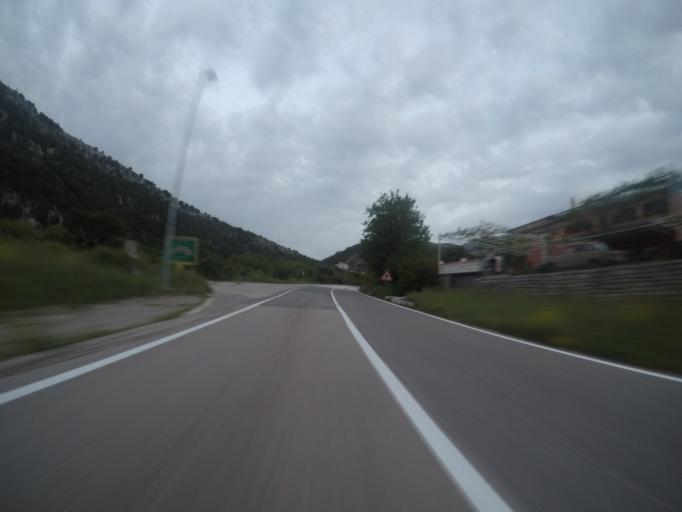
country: ME
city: Petrovac na Moru
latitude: 42.2016
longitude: 18.9614
